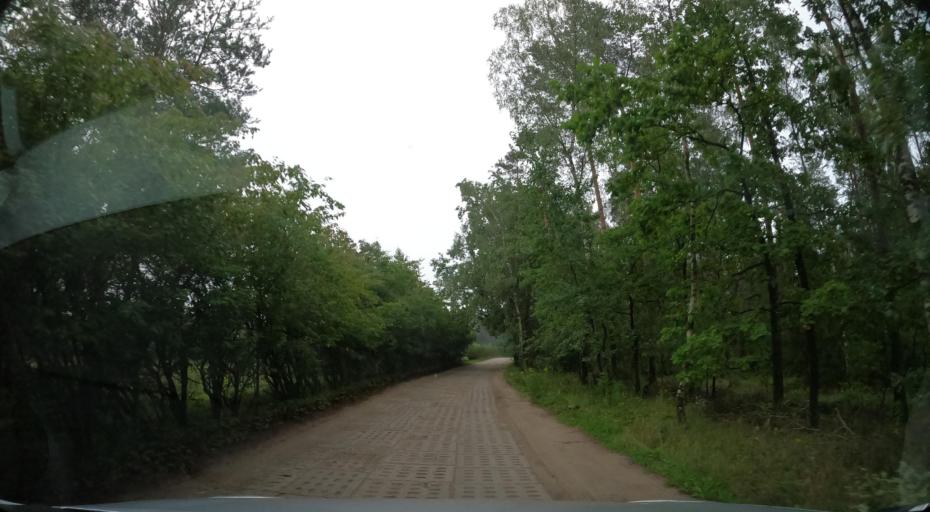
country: PL
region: Pomeranian Voivodeship
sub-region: Powiat kartuski
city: Chwaszczyno
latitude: 54.4210
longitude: 18.4197
